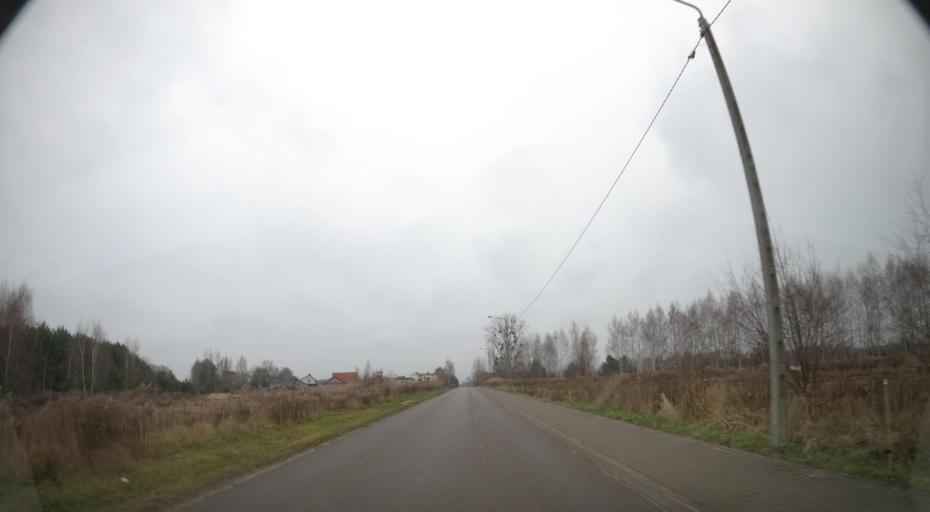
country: PL
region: Masovian Voivodeship
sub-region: Powiat radomski
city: Skaryszew
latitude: 51.3886
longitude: 21.2599
